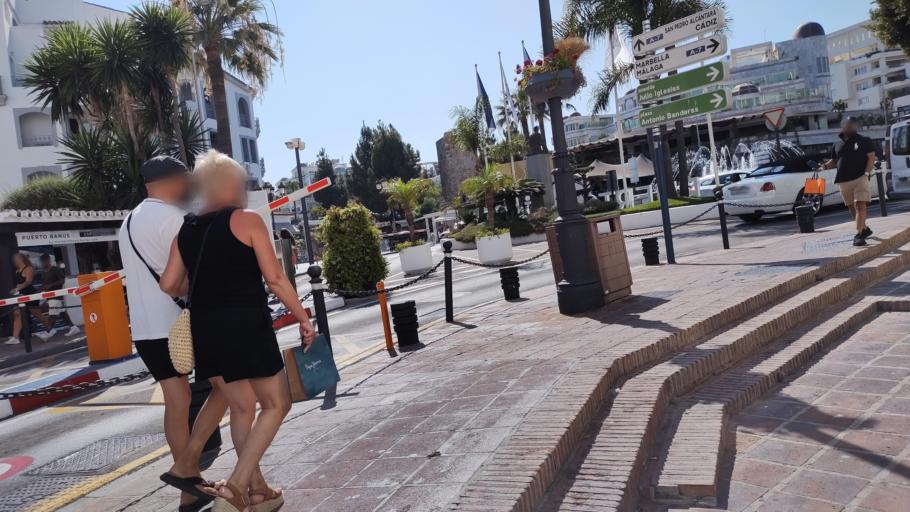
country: ES
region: Andalusia
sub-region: Provincia de Malaga
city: Marbella
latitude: 36.4863
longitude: -4.9550
